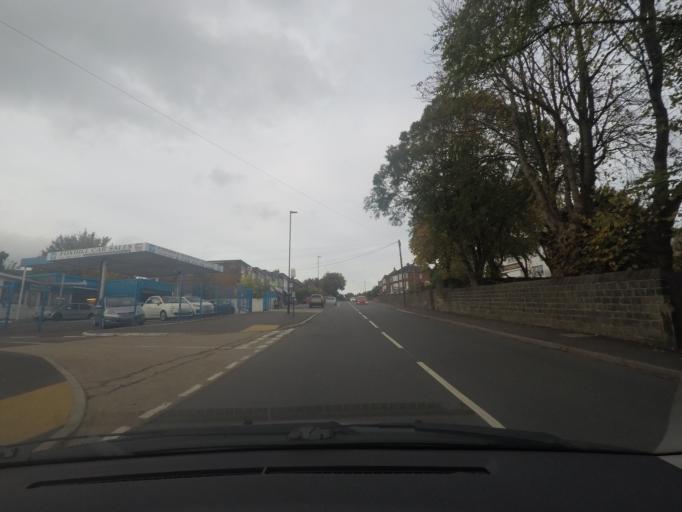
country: GB
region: England
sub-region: Sheffield
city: Oughtibridge
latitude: 53.4251
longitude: -1.5008
